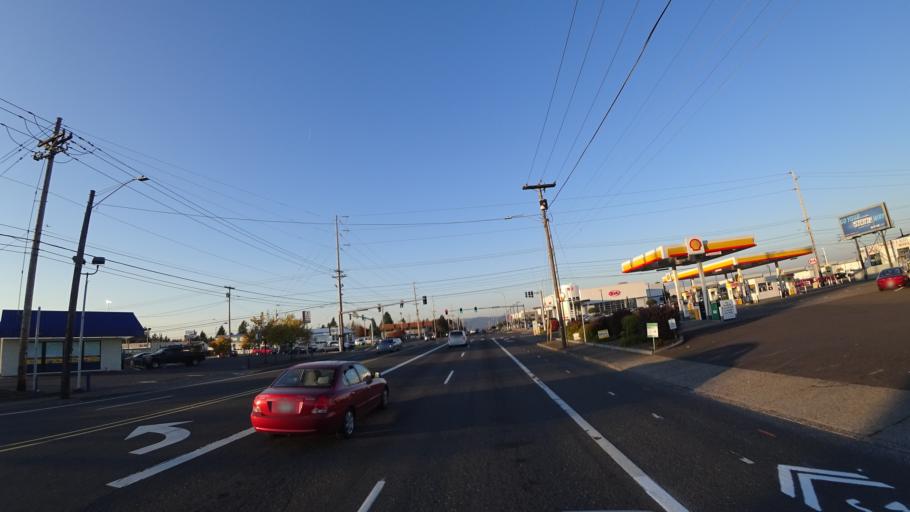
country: US
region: Oregon
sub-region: Multnomah County
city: Fairview
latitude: 45.5184
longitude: -122.4337
